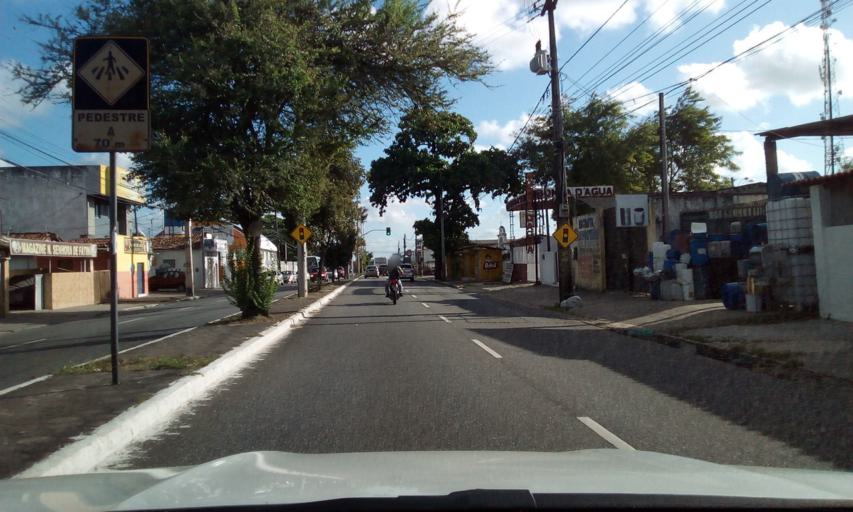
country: BR
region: Paraiba
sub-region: Joao Pessoa
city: Joao Pessoa
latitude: -7.1488
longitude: -34.8933
